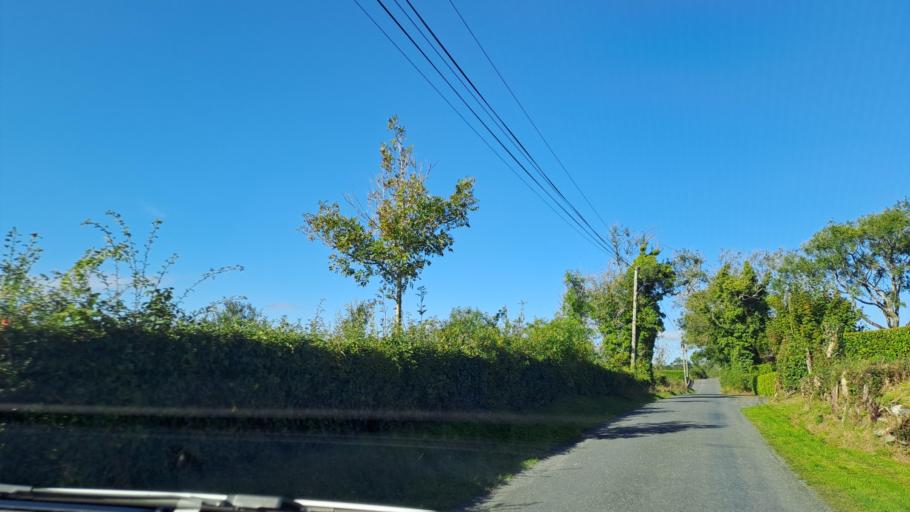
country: IE
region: Ulster
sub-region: County Monaghan
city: Carrickmacross
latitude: 53.9970
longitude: -6.7669
